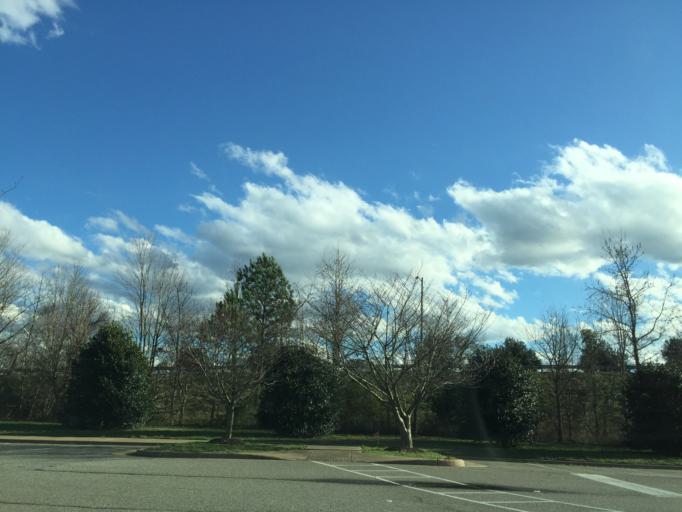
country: US
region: Virginia
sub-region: York County
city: Yorktown
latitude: 37.1262
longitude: -76.5165
